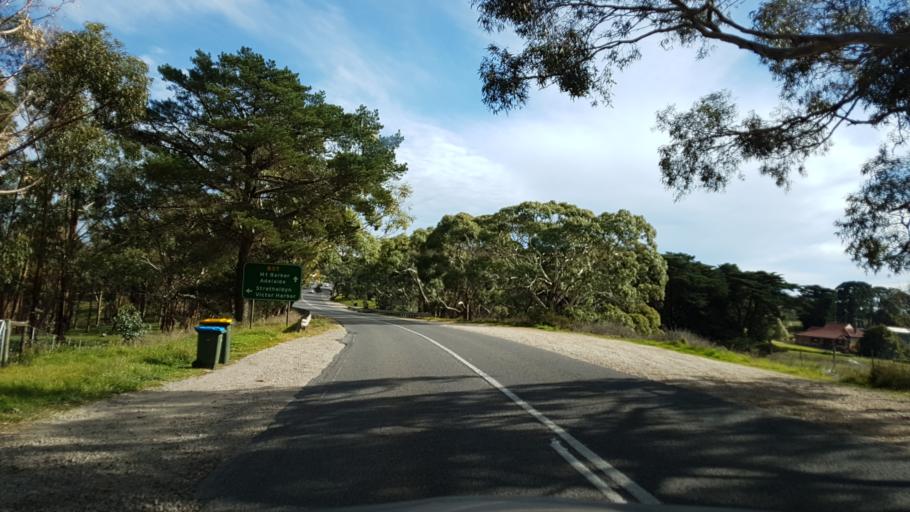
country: AU
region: South Australia
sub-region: Mount Barker
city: Mount Barker
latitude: -35.1147
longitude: 138.8923
